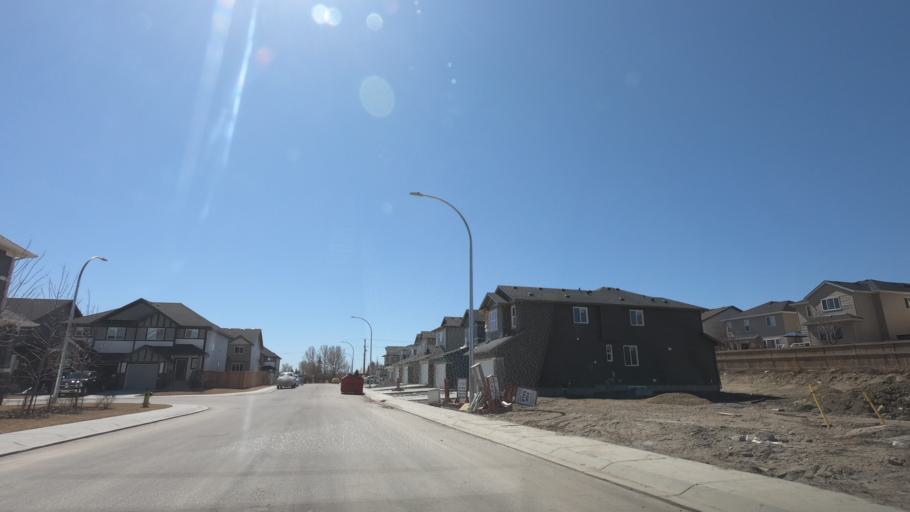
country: CA
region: Alberta
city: Airdrie
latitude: 51.3017
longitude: -114.0452
